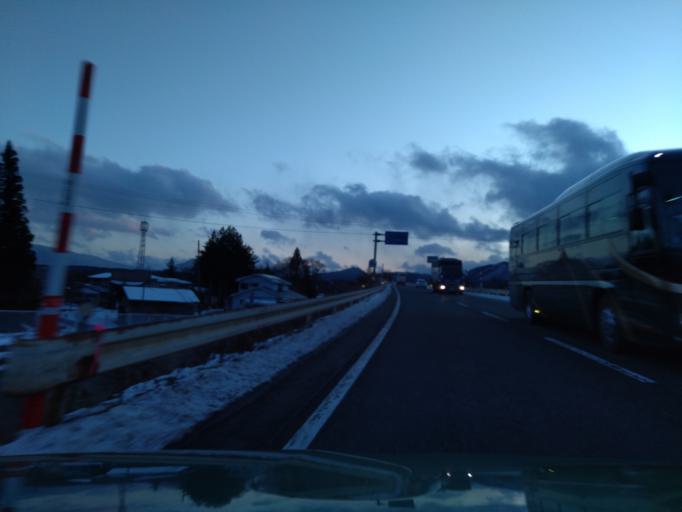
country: JP
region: Iwate
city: Shizukuishi
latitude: 39.6958
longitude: 140.9367
